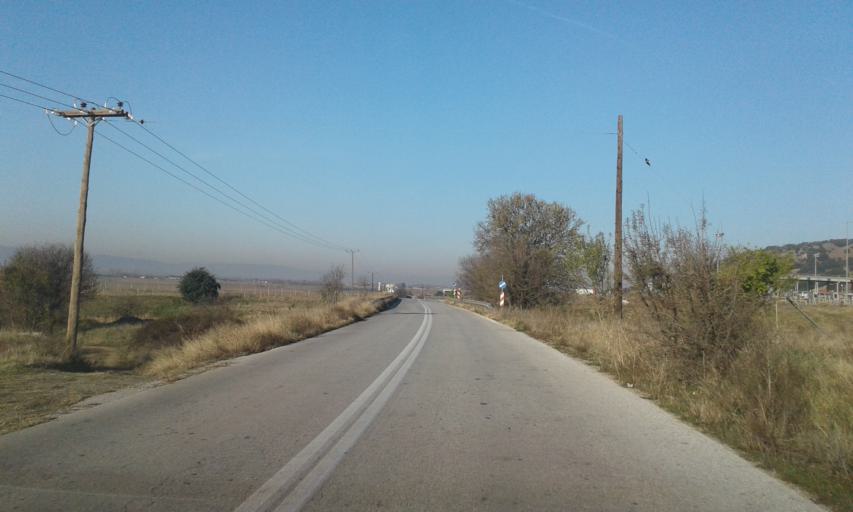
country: GR
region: Central Macedonia
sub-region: Nomos Thessalonikis
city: Kolchikon
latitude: 40.7052
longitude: 23.1936
